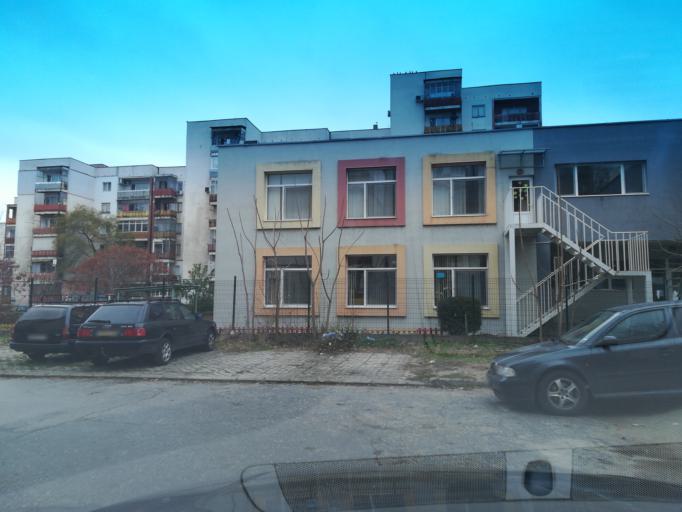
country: BG
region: Plovdiv
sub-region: Obshtina Plovdiv
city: Plovdiv
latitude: 42.1502
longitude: 24.7625
